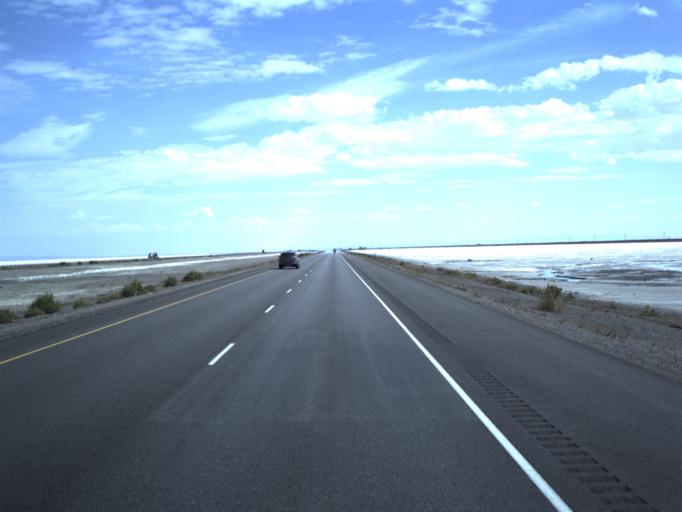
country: US
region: Utah
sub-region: Tooele County
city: Wendover
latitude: 40.7395
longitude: -113.9037
